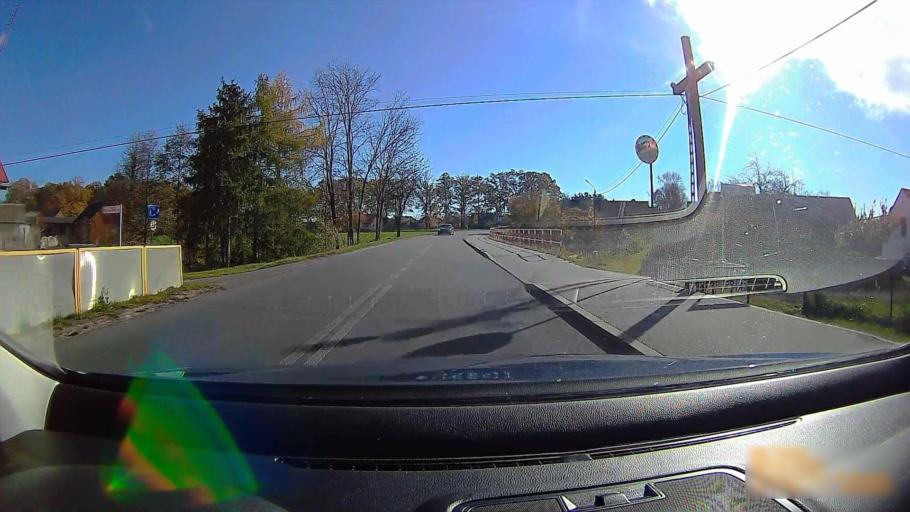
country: PL
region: Greater Poland Voivodeship
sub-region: Powiat ostrzeszowski
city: Doruchow
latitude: 51.3609
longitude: 18.0291
